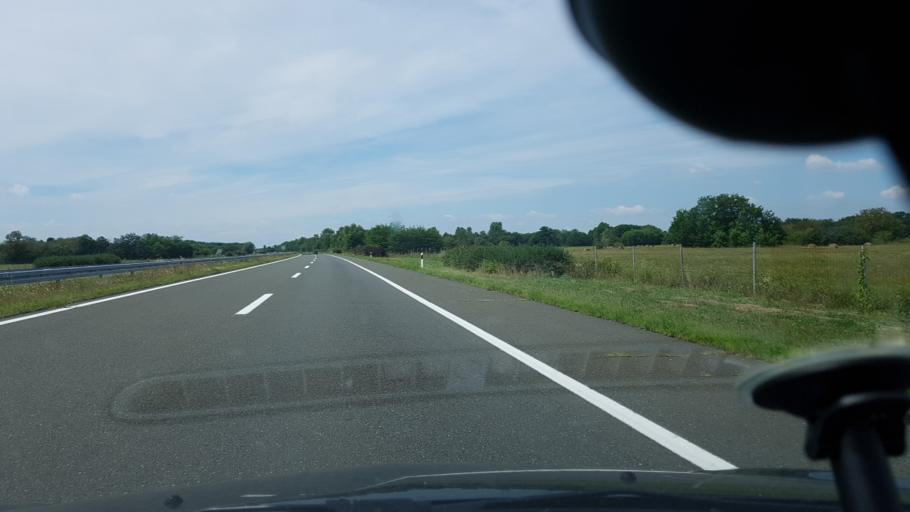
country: HR
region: Medimurska
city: Hodosan
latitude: 46.4134
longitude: 16.6251
